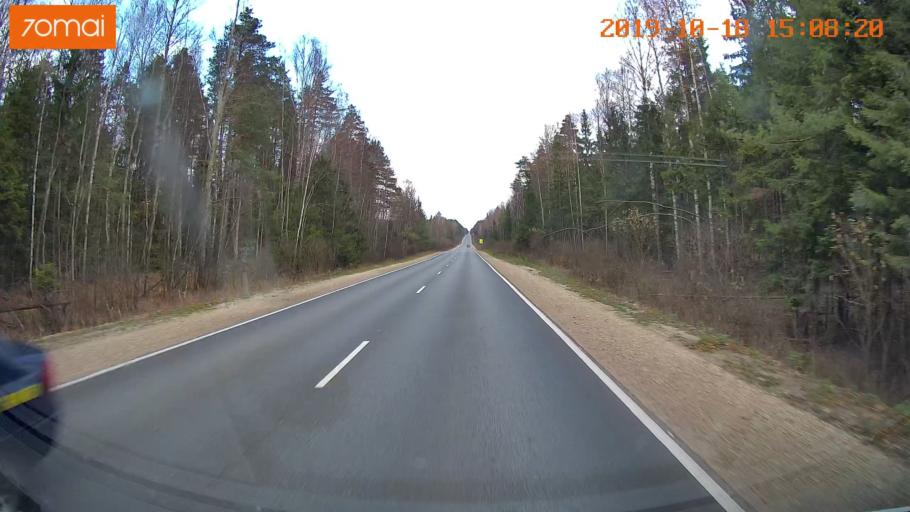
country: RU
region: Vladimir
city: Gus'-Khrustal'nyy
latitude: 55.5509
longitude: 40.6094
